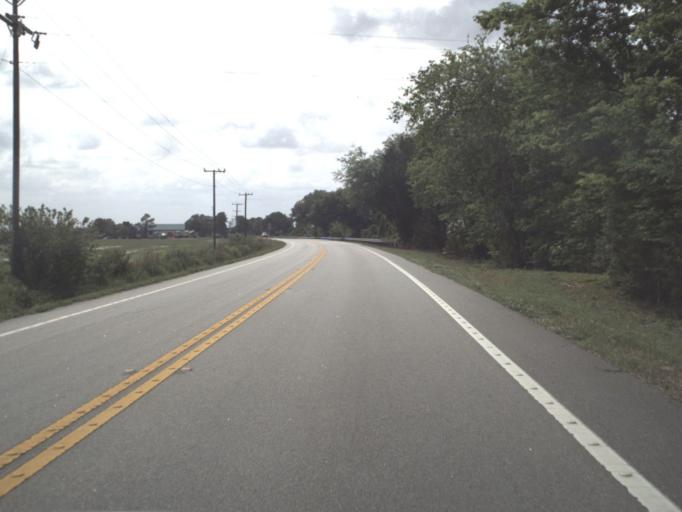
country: US
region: Florida
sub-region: Flagler County
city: Bunnell
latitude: 29.4822
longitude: -81.3493
